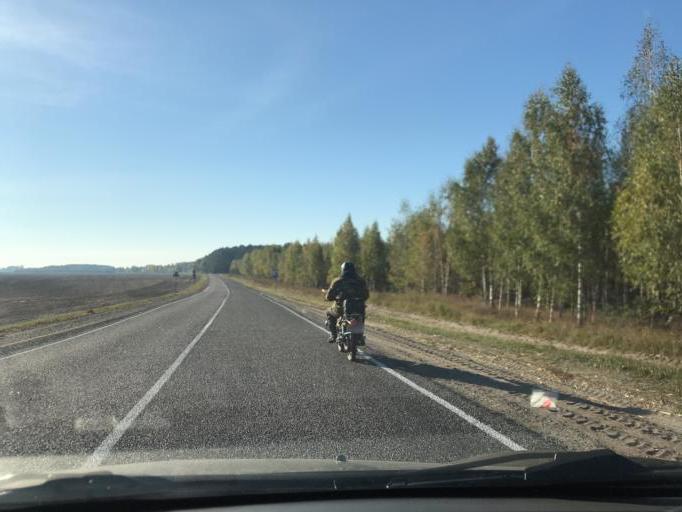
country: BY
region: Gomel
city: Brahin
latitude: 51.7674
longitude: 30.3014
